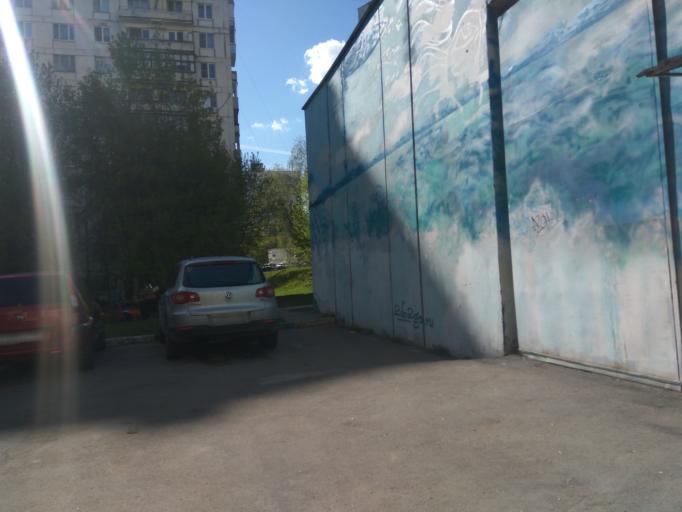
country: RU
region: Moscow
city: Kolomenskoye
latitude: 55.6769
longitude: 37.6767
